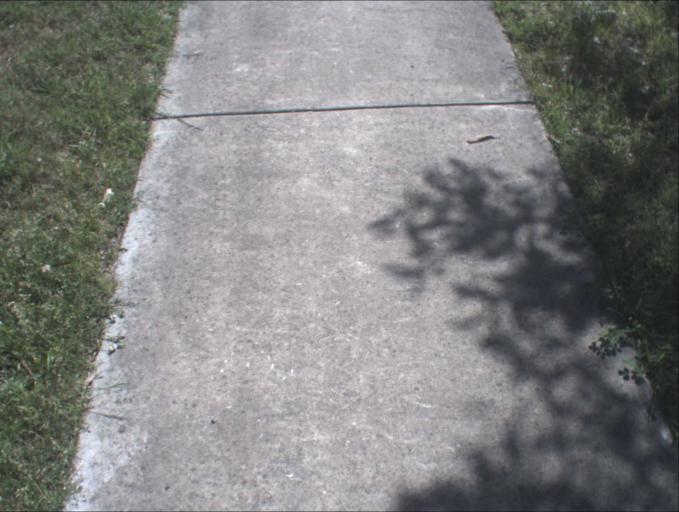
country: AU
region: Queensland
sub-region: Logan
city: Park Ridge South
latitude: -27.7432
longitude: 153.0496
